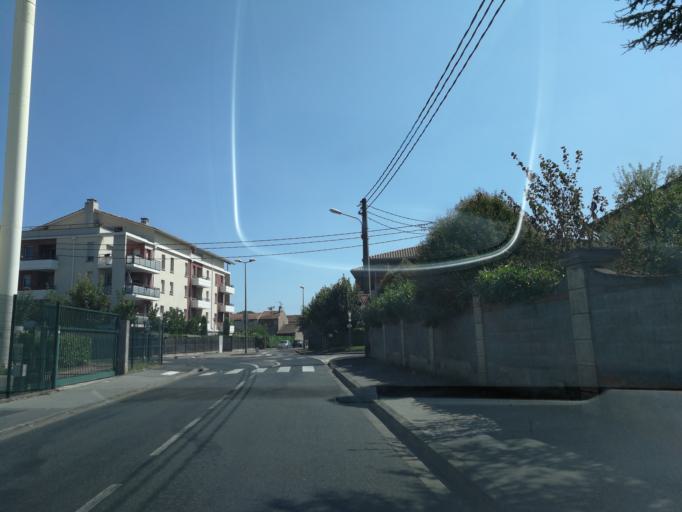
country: FR
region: Midi-Pyrenees
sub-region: Departement de la Haute-Garonne
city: Toulouse
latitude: 43.6336
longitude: 1.4574
